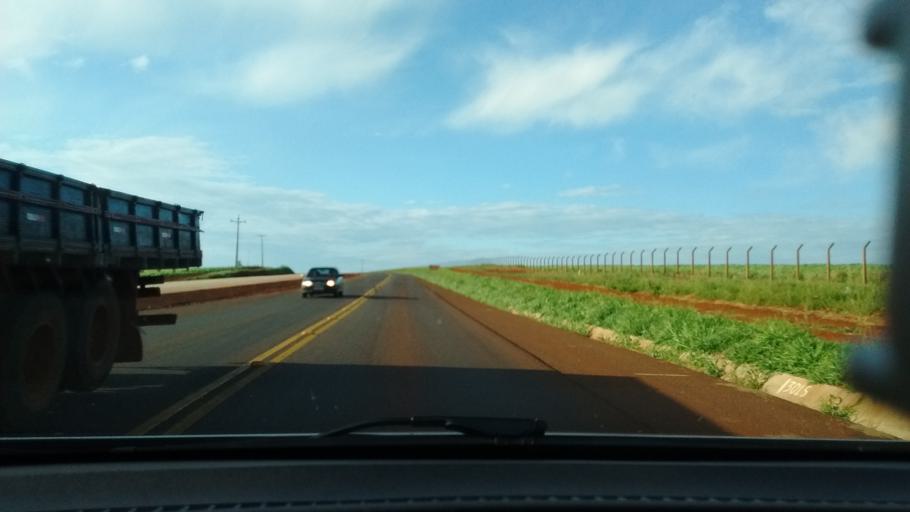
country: BR
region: Parana
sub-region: Cascavel
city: Cascavel
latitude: -25.1247
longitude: -53.5877
